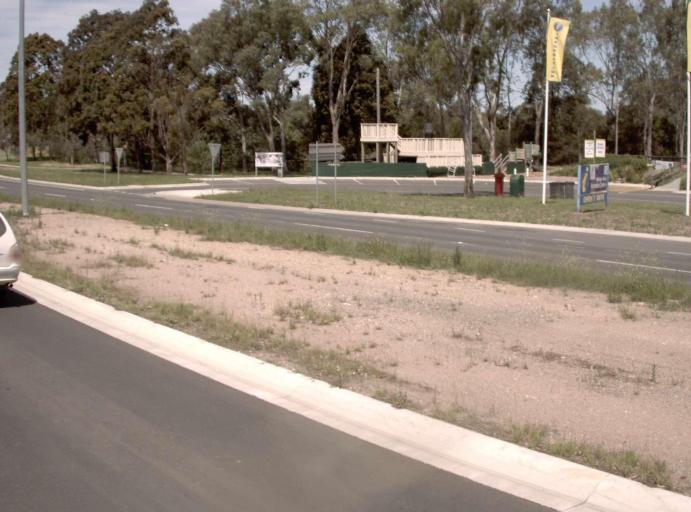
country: AU
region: Victoria
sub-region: Wellington
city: Sale
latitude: -38.1120
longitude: 147.0571
